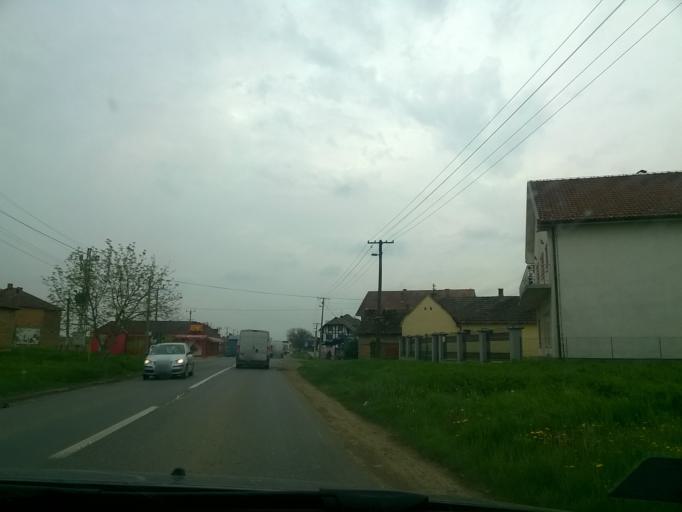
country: RS
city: Platicevo
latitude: 44.8274
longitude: 19.7787
